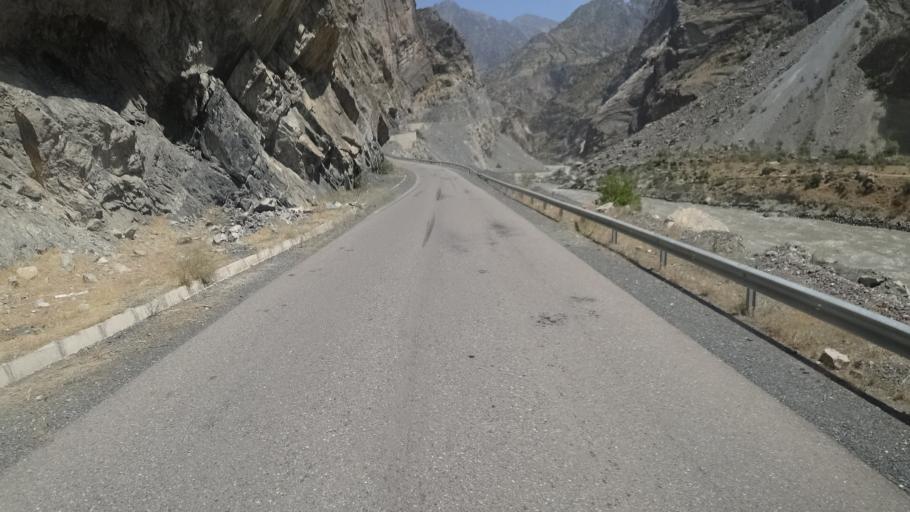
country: AF
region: Badakhshan
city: Deh Khwahan
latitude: 37.9984
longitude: 70.3131
